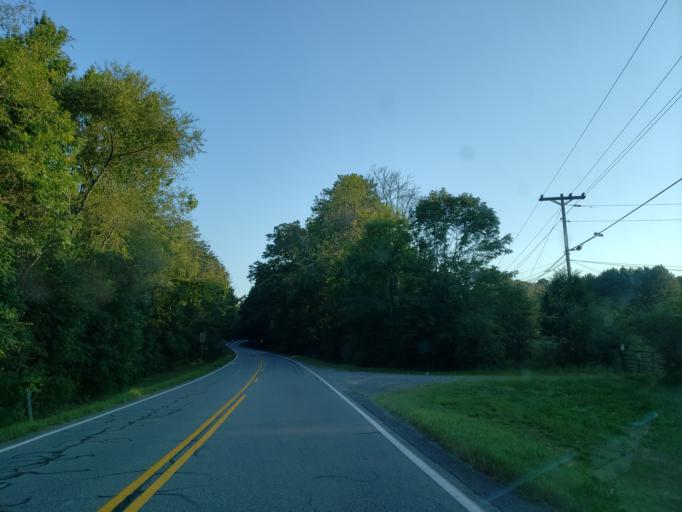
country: US
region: Georgia
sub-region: Gordon County
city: Calhoun
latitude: 34.5519
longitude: -84.8947
